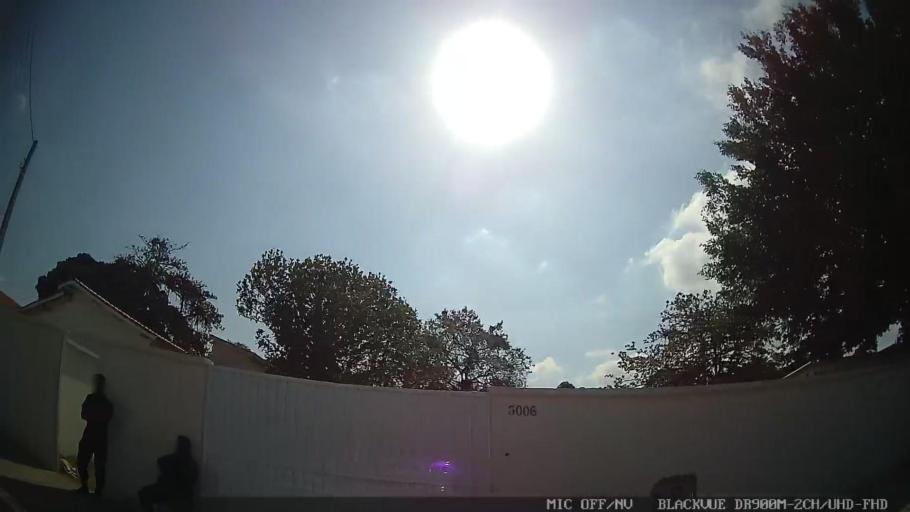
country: BR
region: Sao Paulo
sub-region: Santos
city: Santos
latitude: -23.9389
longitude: -46.2991
